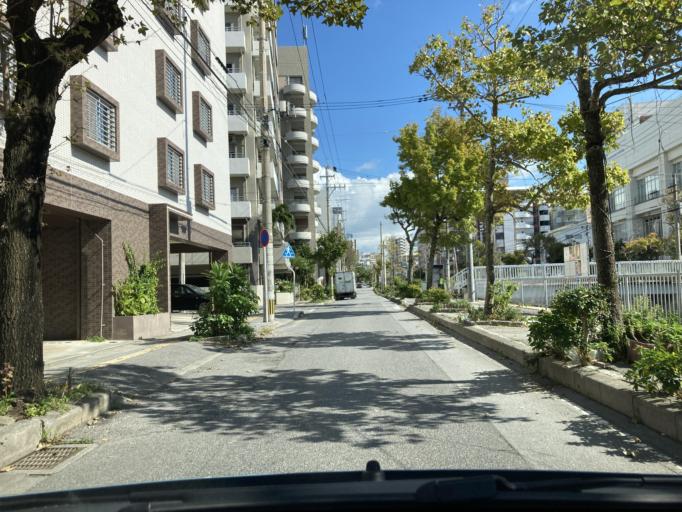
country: JP
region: Okinawa
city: Naha-shi
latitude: 26.2221
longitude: 127.6805
